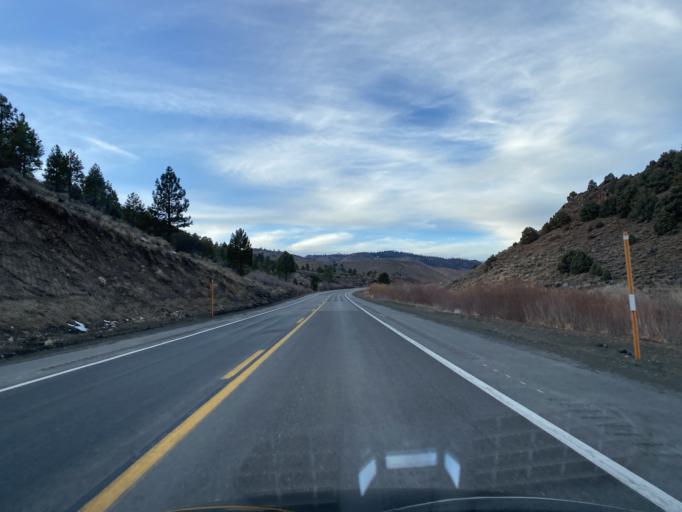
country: US
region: California
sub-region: Mono County
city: Bridgeport
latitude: 38.2907
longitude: -119.3075
